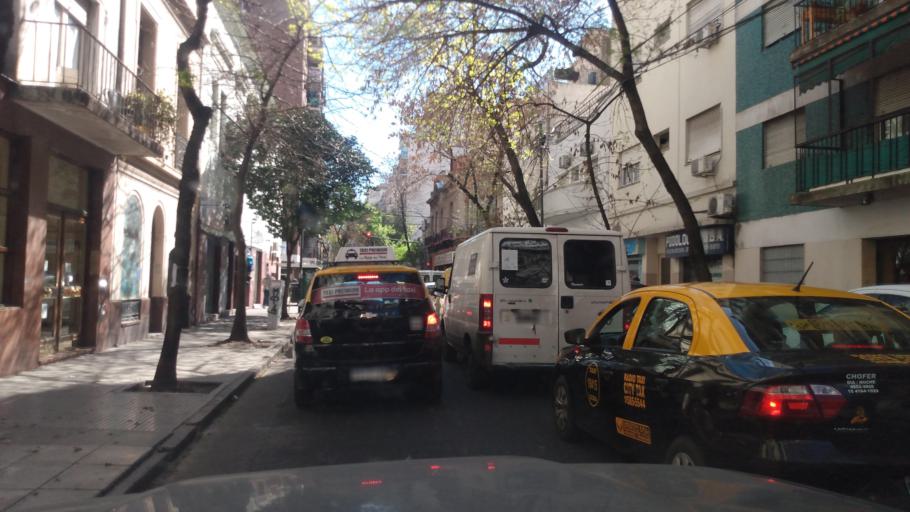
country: AR
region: Buenos Aires F.D.
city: Buenos Aires
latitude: -34.6121
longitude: -58.3947
